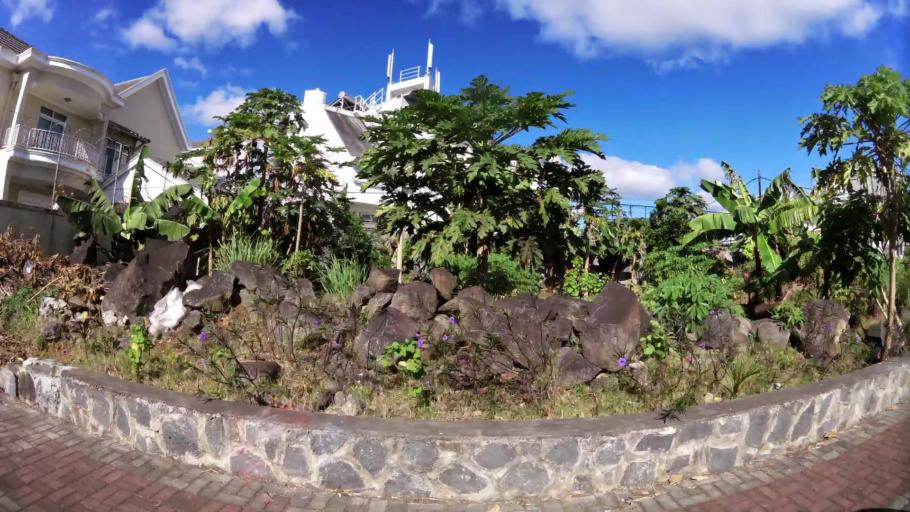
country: MU
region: Plaines Wilhems
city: Quatre Bornes
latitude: -20.2689
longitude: 57.4879
